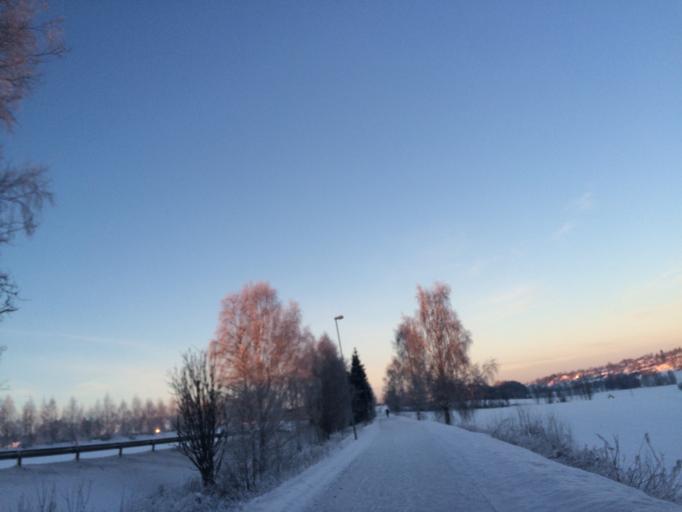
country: NO
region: Akershus
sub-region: Ski
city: Ski
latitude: 59.6976
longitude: 10.8328
